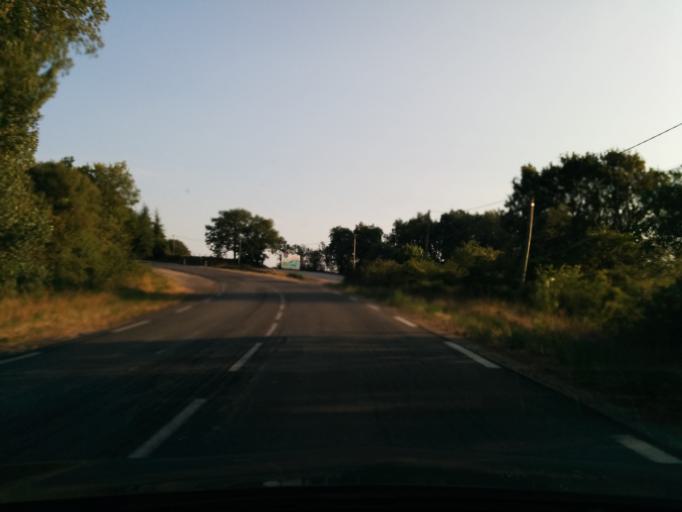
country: FR
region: Midi-Pyrenees
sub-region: Departement du Lot
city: Le Vigan
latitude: 44.6234
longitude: 1.4895
